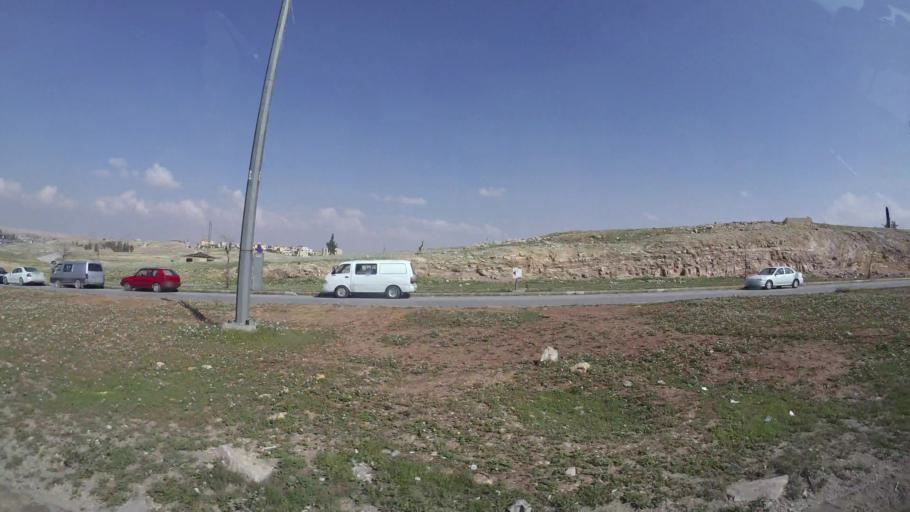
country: JO
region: Zarqa
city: Zarqa
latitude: 32.0746
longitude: 36.1036
